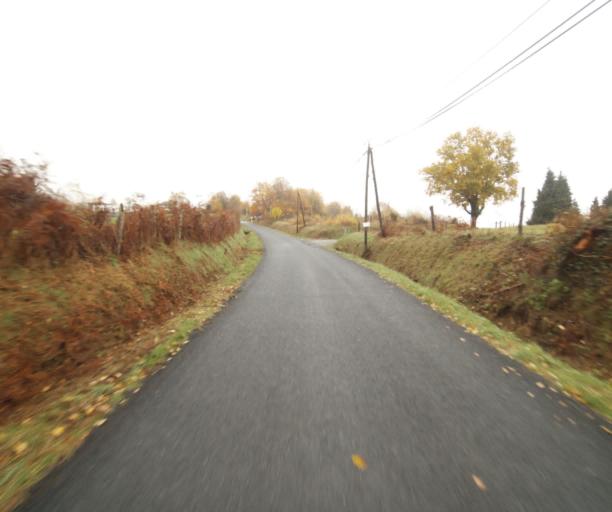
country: FR
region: Limousin
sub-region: Departement de la Correze
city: Sainte-Fereole
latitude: 45.1906
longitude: 1.6279
